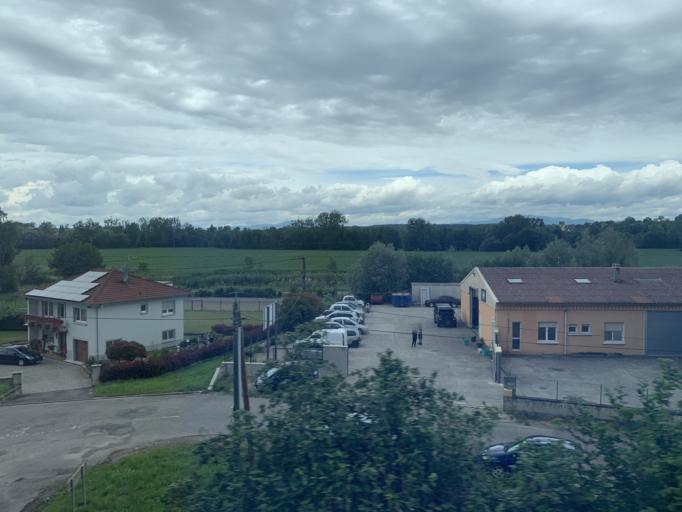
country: FR
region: Alsace
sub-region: Departement du Haut-Rhin
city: Illfurth
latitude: 47.6836
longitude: 7.2763
